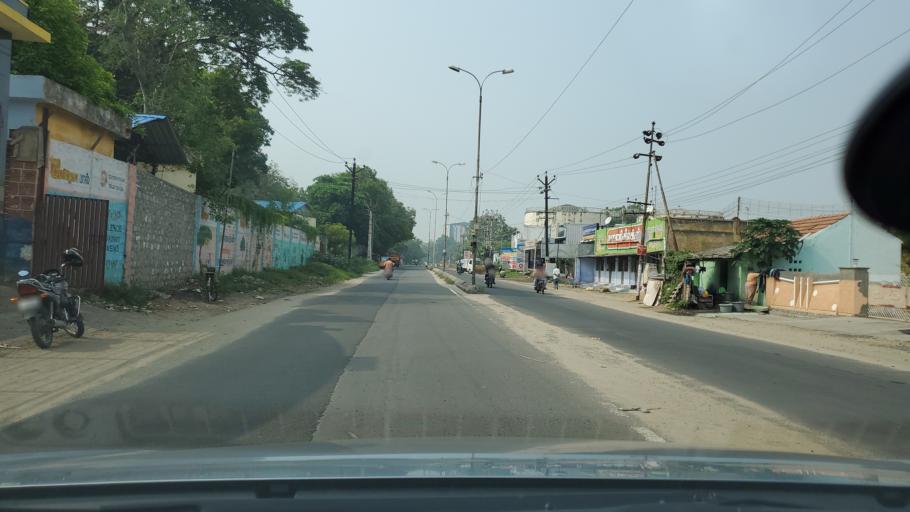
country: IN
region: Tamil Nadu
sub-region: Erode
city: Erode
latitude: 11.3249
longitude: 77.7170
